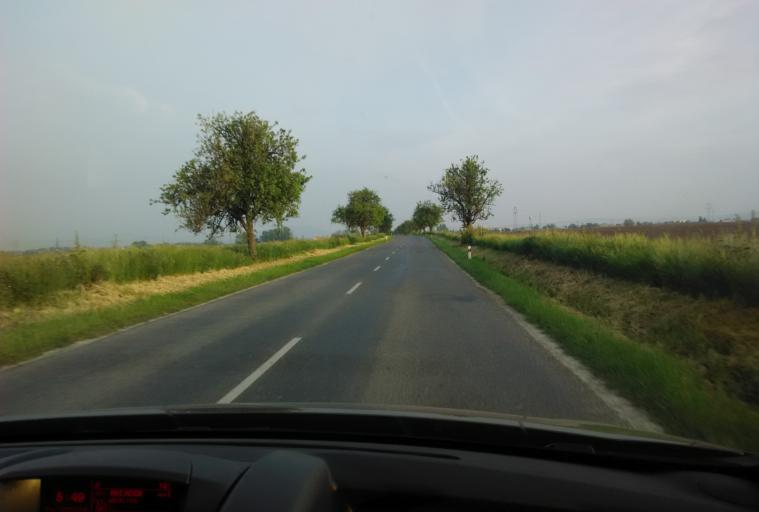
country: SK
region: Trnavsky
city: Leopoldov
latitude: 48.4426
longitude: 17.6961
